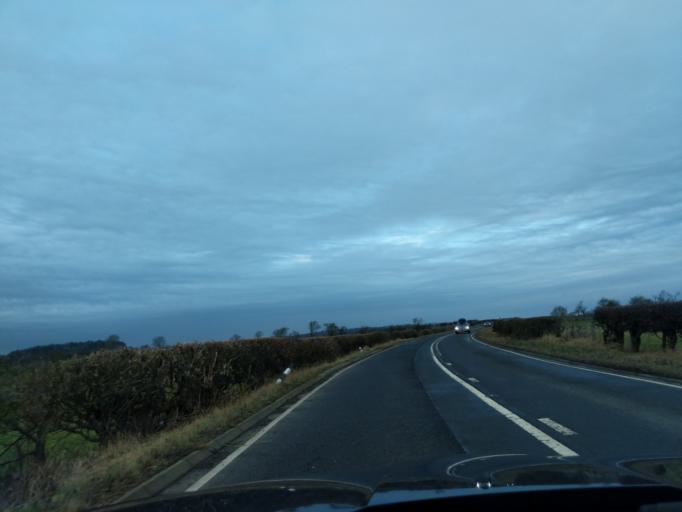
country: GB
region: England
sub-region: Northumberland
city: Rothley
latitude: 55.1158
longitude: -1.8996
